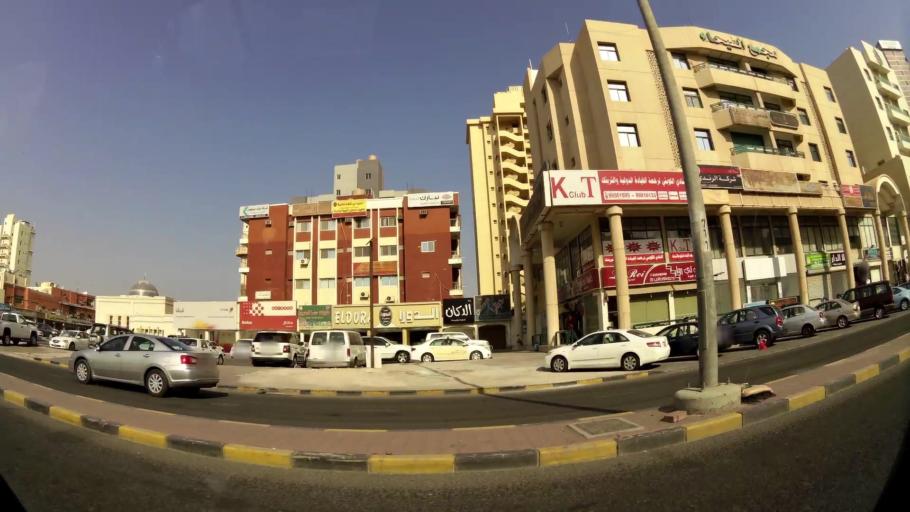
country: KW
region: Muhafazat Hawalli
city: Hawalli
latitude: 29.3382
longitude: 48.0048
